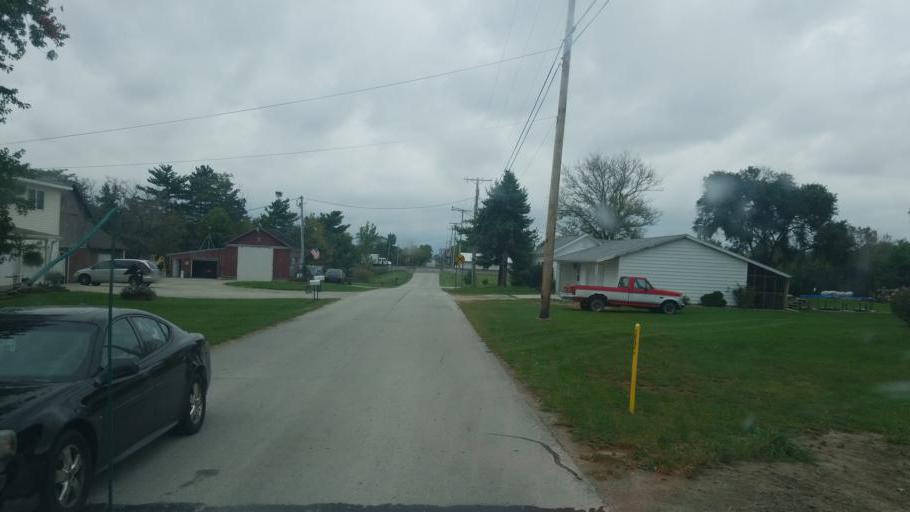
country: US
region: Ohio
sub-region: Seneca County
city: Fostoria
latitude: 41.1107
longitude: -83.5163
